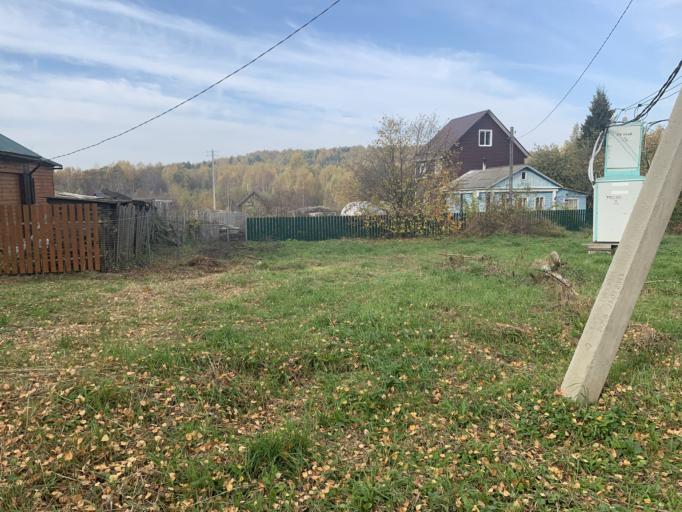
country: RU
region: Jaroslavl
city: Porech'ye-Rybnoye
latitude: 56.9806
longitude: 39.3839
